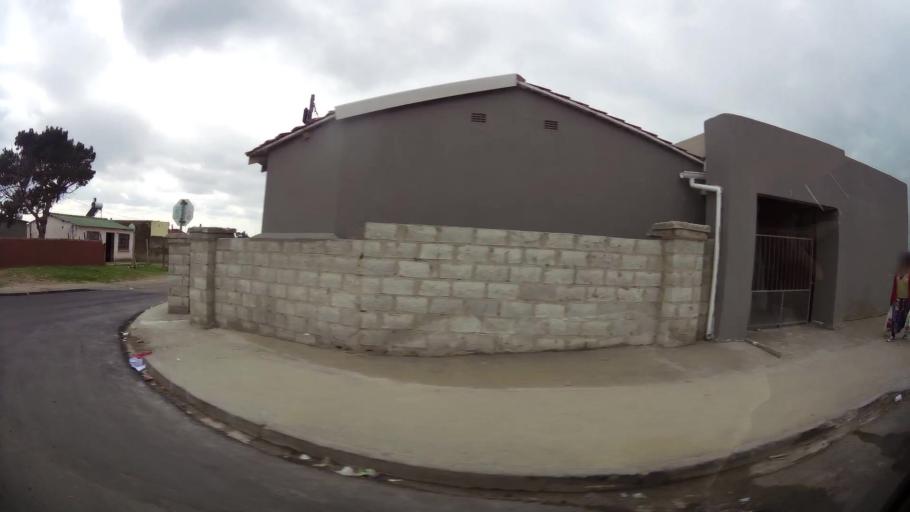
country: ZA
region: Eastern Cape
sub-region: Nelson Mandela Bay Metropolitan Municipality
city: Port Elizabeth
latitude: -33.8730
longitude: 25.5841
